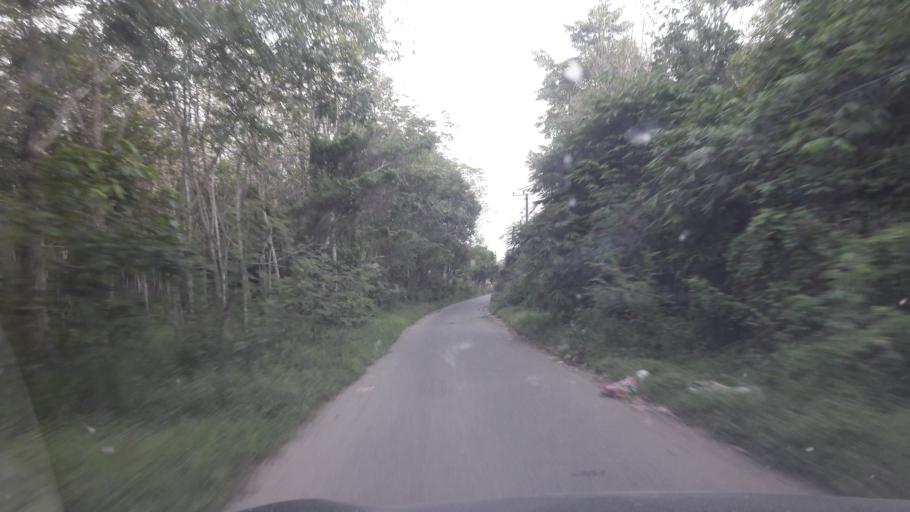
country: ID
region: South Sumatra
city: Gunungmenang
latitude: -3.3186
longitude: 104.0937
